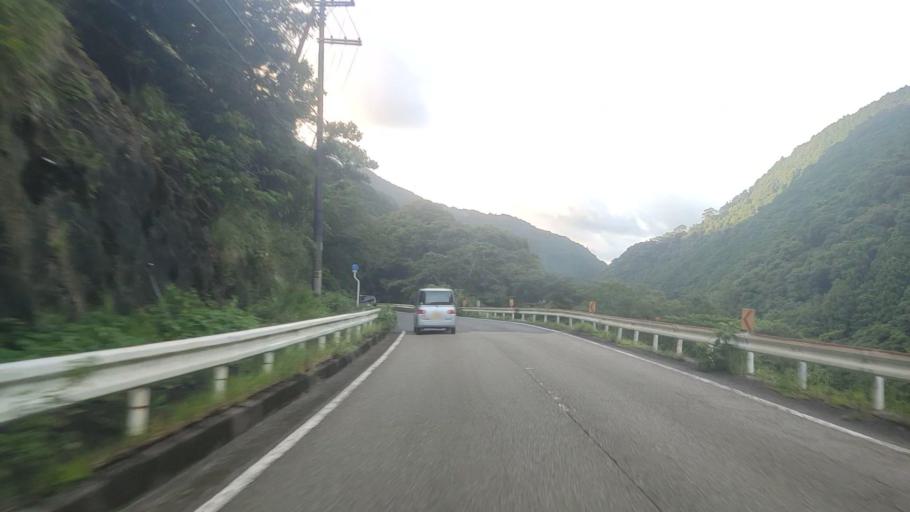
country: JP
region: Wakayama
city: Tanabe
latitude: 33.7654
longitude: 135.5001
